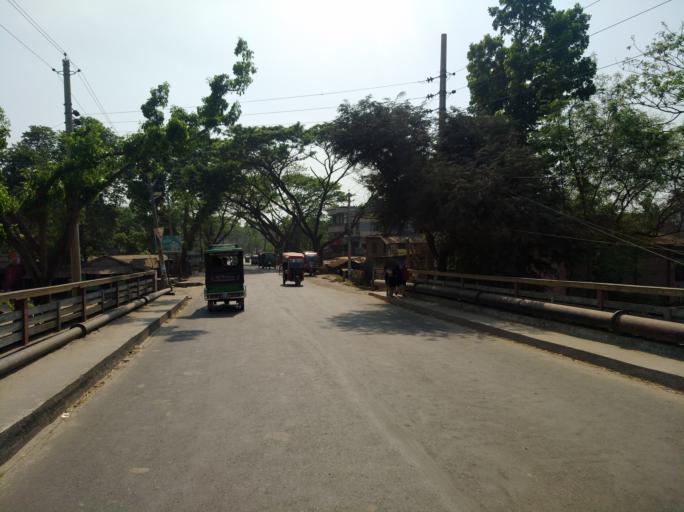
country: BD
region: Khulna
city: Kaliganj
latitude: 23.5495
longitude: 89.1685
